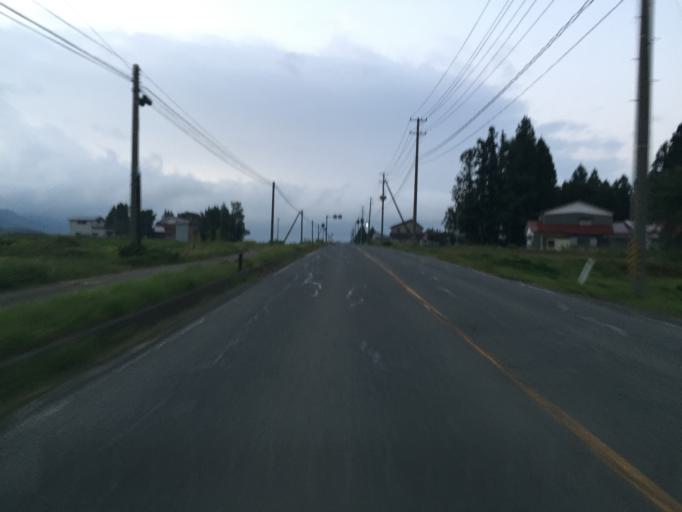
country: JP
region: Fukushima
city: Inawashiro
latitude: 37.5765
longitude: 140.1260
